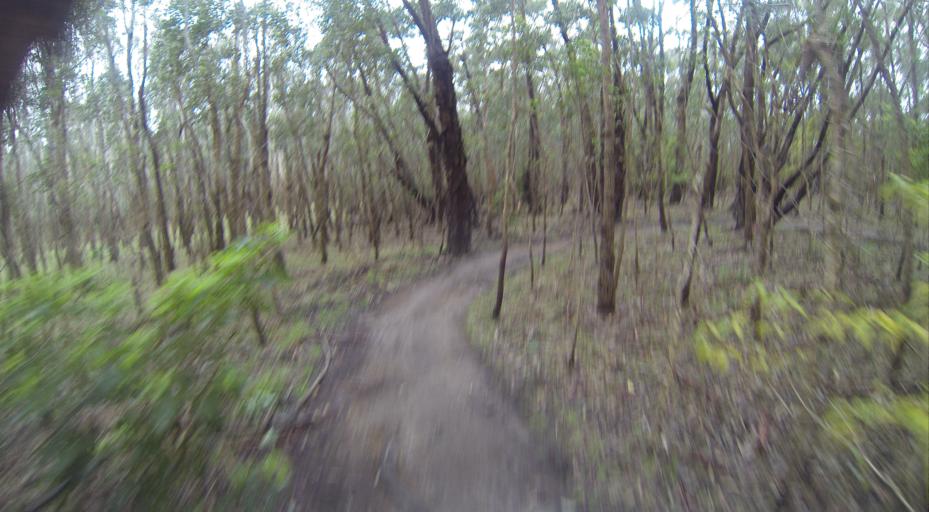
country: AU
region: Victoria
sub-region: Yarra Ranges
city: Lysterfield
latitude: -37.9396
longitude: 145.3032
